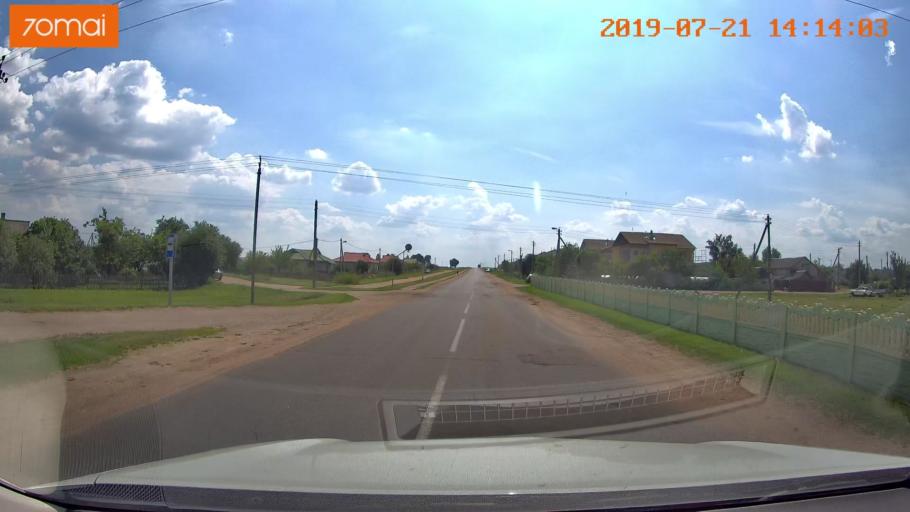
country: BY
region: Grodnenskaya
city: Karelichy
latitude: 53.6507
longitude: 26.1695
